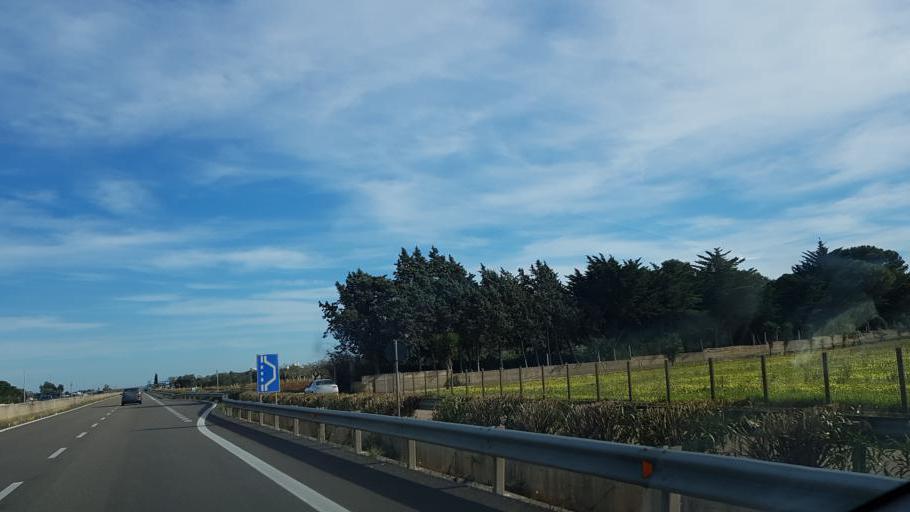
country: IT
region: Apulia
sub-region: Provincia di Brindisi
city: Carovigno
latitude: 40.7393
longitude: 17.7196
